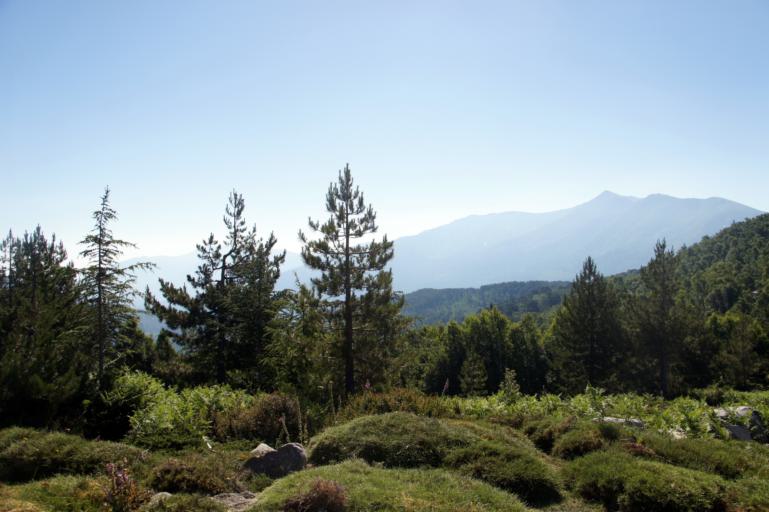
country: FR
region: Corsica
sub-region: Departement de la Haute-Corse
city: Calenzana
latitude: 42.2905
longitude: 8.8783
